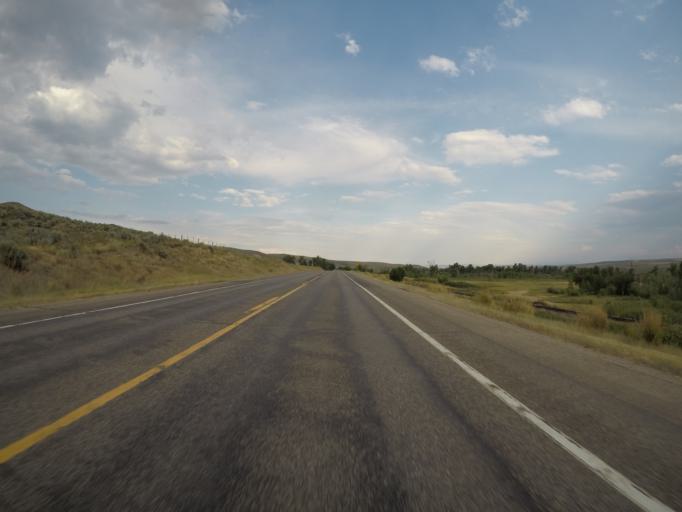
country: US
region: Colorado
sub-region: Moffat County
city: Craig
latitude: 40.5252
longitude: -107.4095
